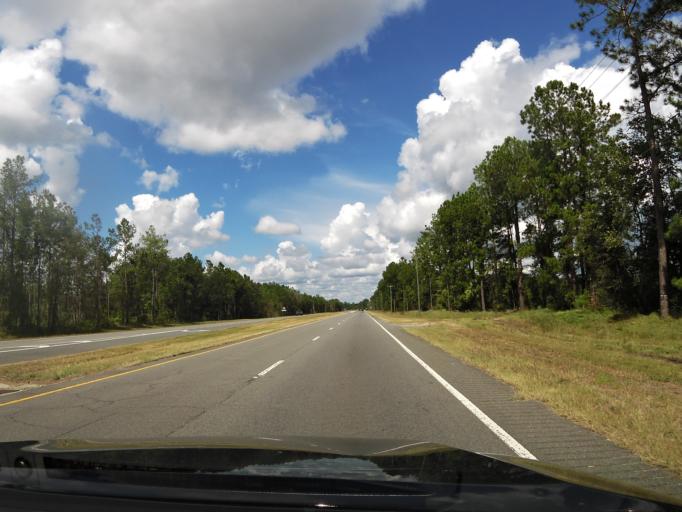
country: US
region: Georgia
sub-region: Charlton County
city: Folkston
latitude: 30.7883
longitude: -81.9817
